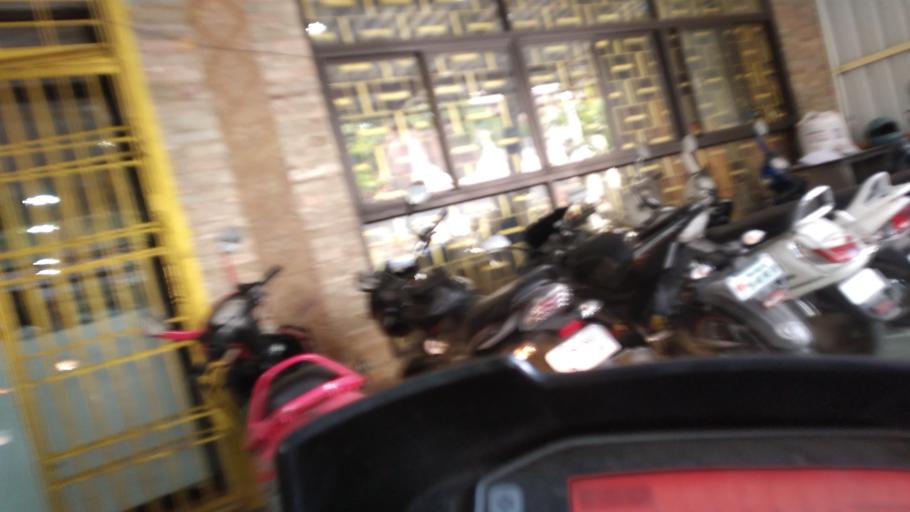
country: IN
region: Tamil Nadu
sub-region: Salem
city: Salem
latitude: 11.6762
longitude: 78.1429
